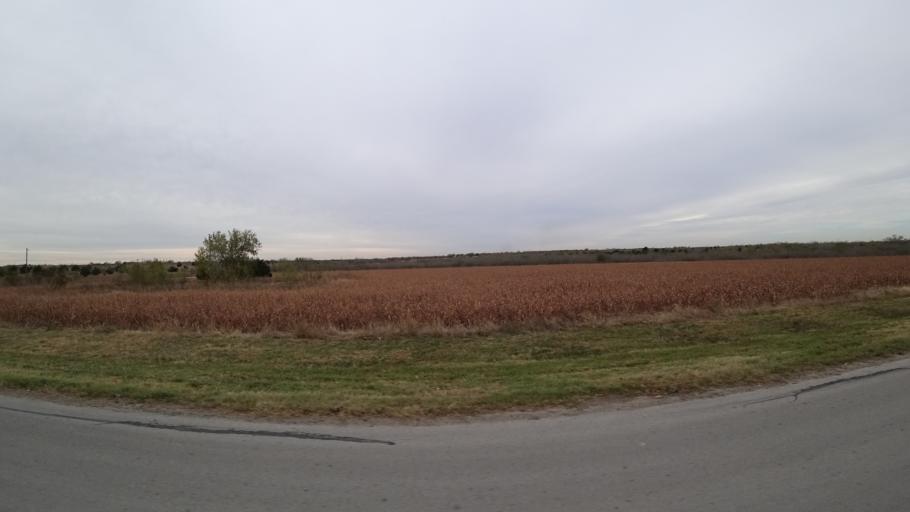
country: US
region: Texas
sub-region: Travis County
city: Garfield
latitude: 30.1109
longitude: -97.6238
